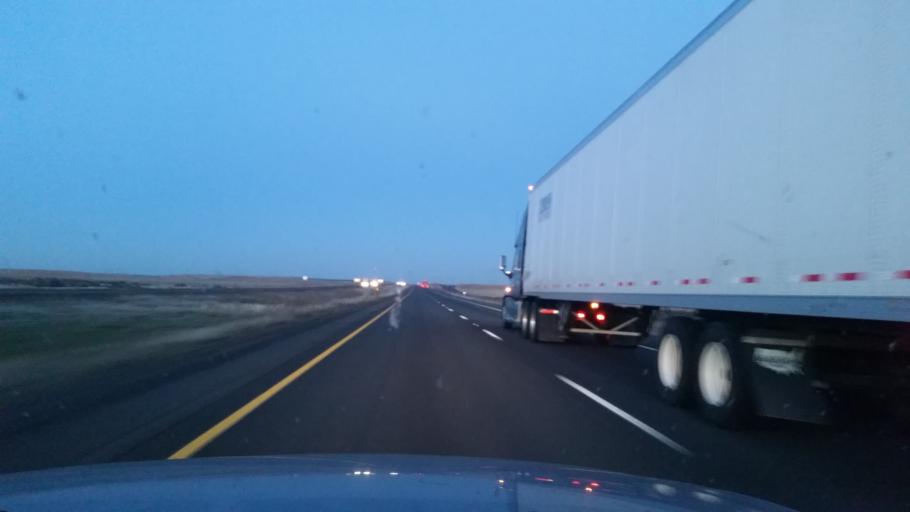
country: US
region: Washington
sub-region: Adams County
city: Ritzville
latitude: 47.1690
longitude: -118.2903
